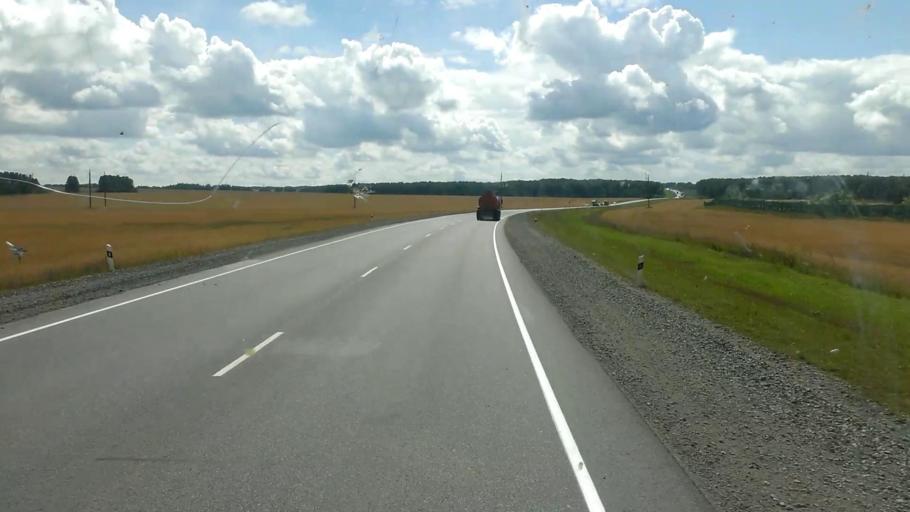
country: RU
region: Altai Krai
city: Troitskoye
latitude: 52.9935
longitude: 84.7409
